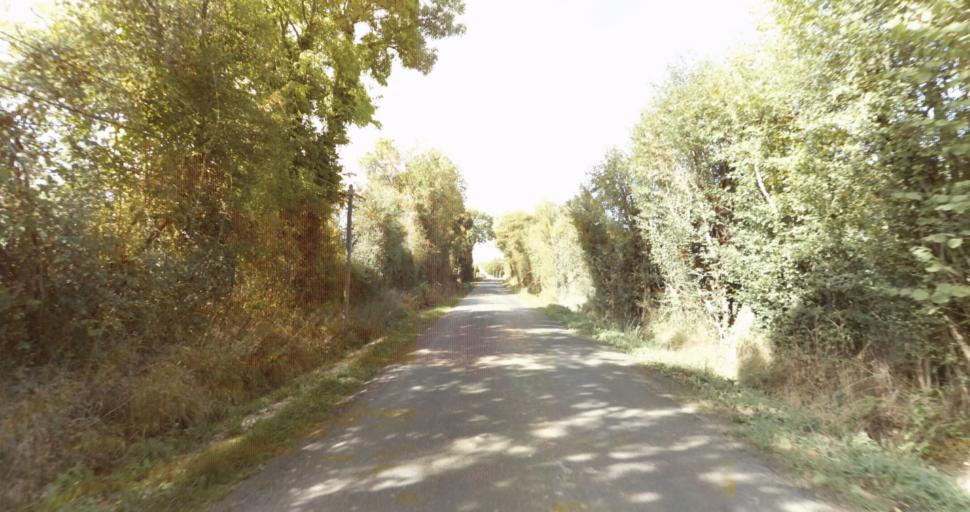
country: FR
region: Lower Normandy
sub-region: Departement de l'Orne
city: Gace
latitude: 48.7279
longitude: 0.2243
